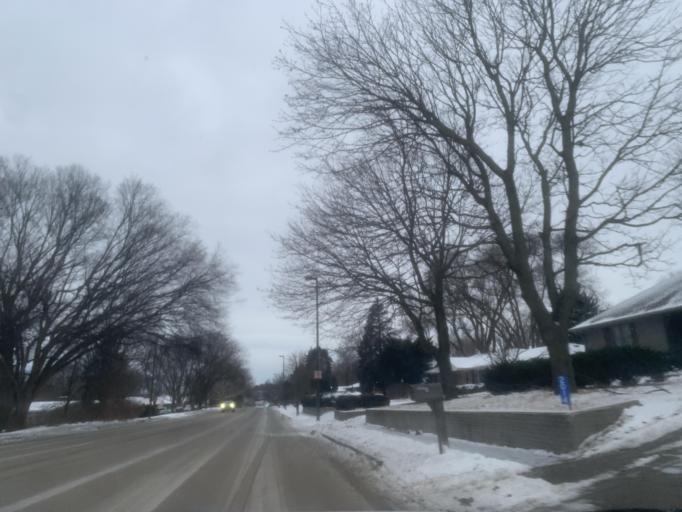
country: US
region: Nebraska
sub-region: Douglas County
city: Ralston
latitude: 41.2406
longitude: -96.0527
